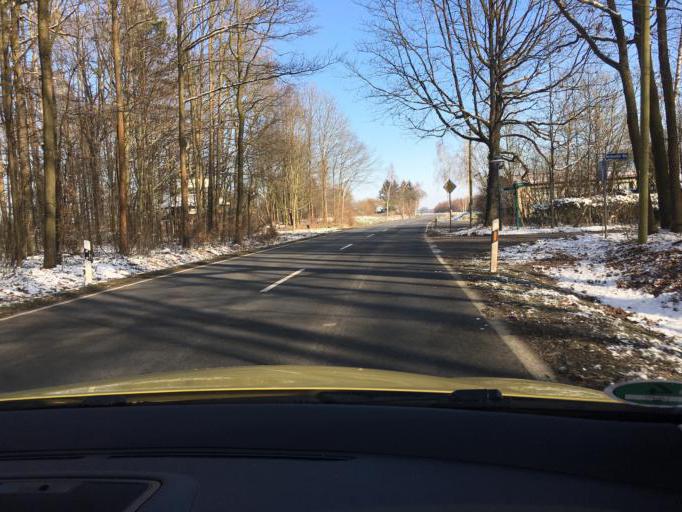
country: DE
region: Saxony
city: Bad Lausick
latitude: 51.1543
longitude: 12.6431
